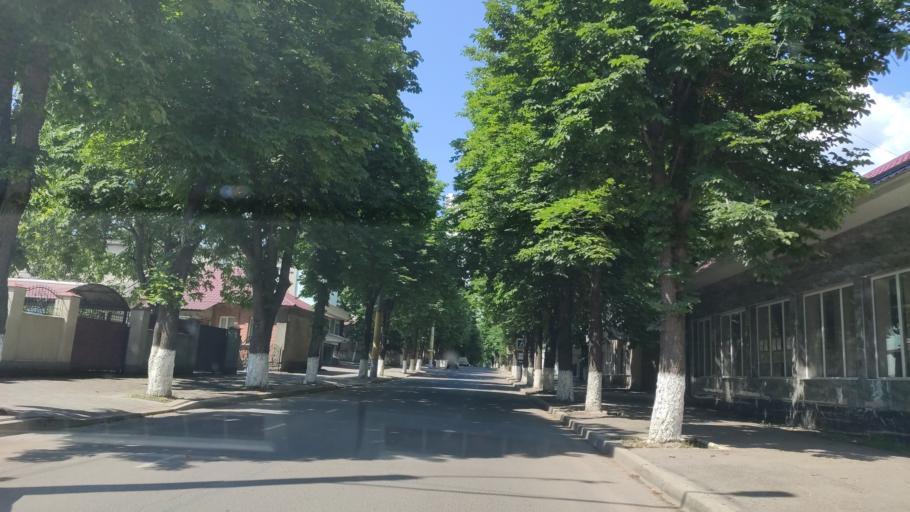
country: MD
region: Raionul Soroca
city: Soroca
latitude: 48.1508
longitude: 28.3022
